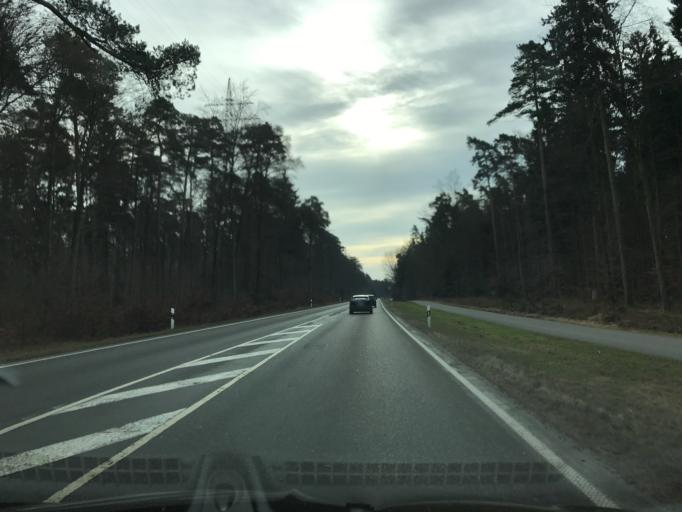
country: DE
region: Baden-Wuerttemberg
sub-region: Tuebingen Region
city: Eriskirch
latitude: 47.6233
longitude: 9.5554
